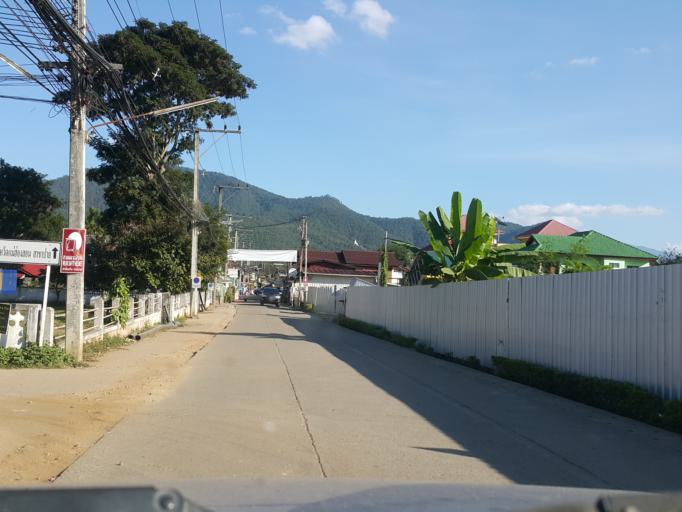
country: TH
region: Chiang Mai
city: Pai
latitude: 19.3617
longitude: 98.4384
